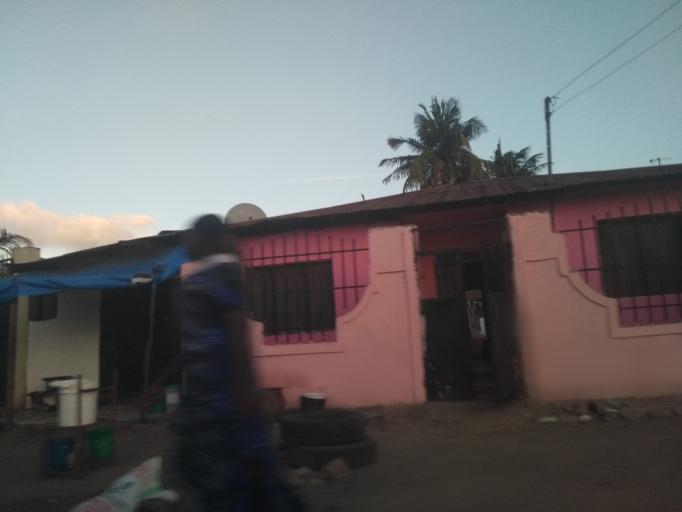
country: TZ
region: Dar es Salaam
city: Dar es Salaam
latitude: -6.8569
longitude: 39.2668
